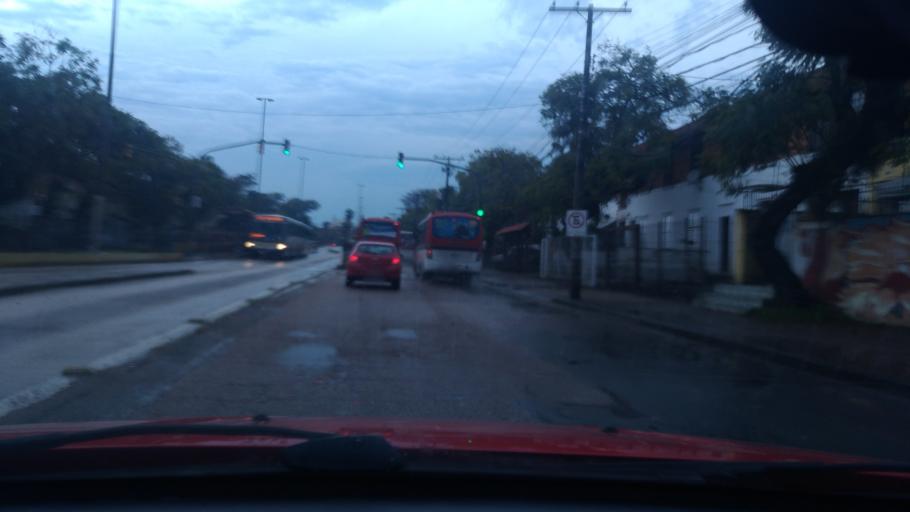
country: BR
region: Rio Grande do Sul
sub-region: Porto Alegre
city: Porto Alegre
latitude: -30.0092
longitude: -51.1783
